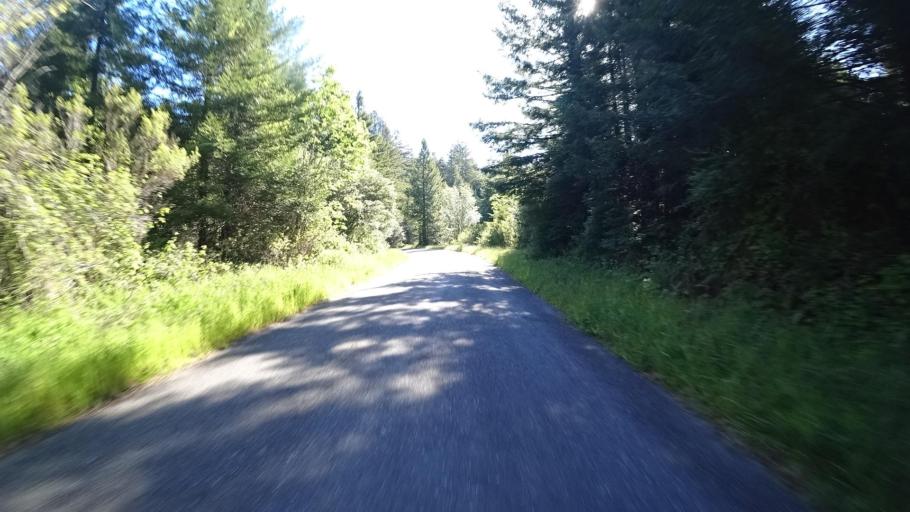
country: US
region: California
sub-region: Humboldt County
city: Rio Dell
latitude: 40.4343
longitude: -123.9657
